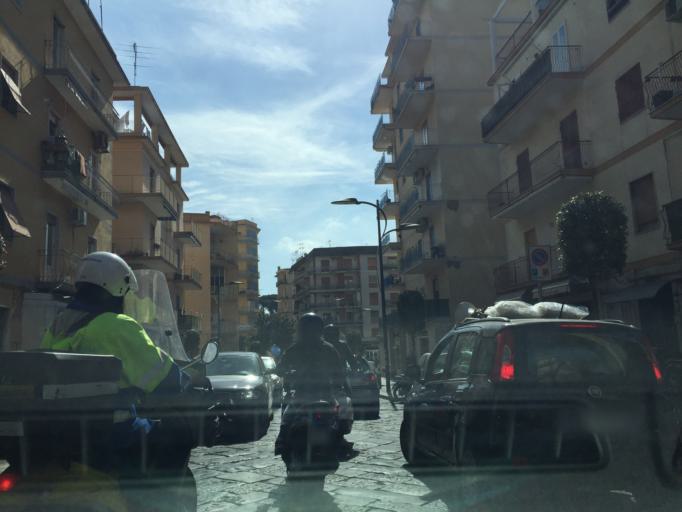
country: IT
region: Campania
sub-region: Provincia di Napoli
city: Ercolano
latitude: 40.8094
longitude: 14.3536
